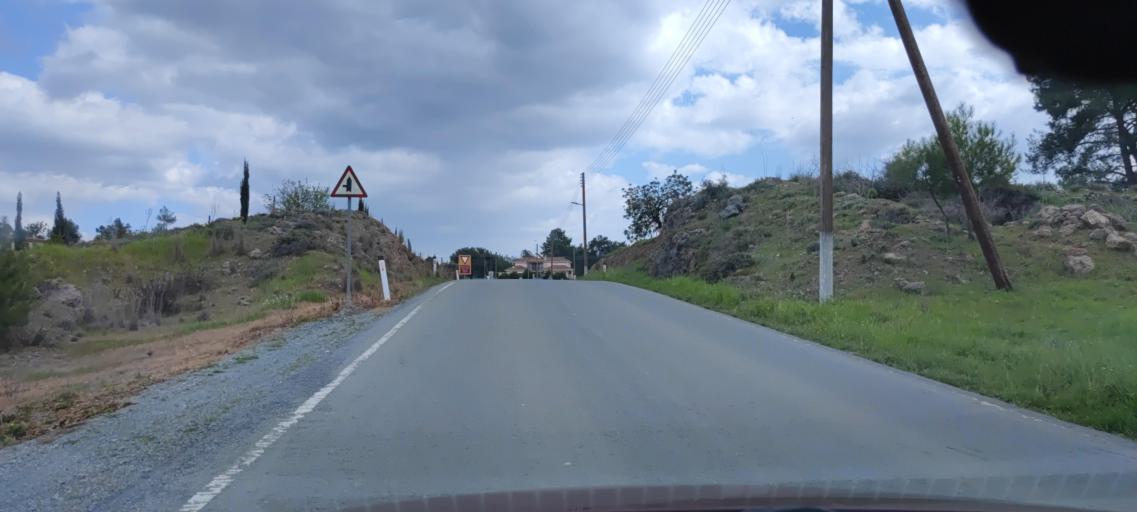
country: CY
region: Larnaka
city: Kornos
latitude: 34.9163
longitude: 33.3609
